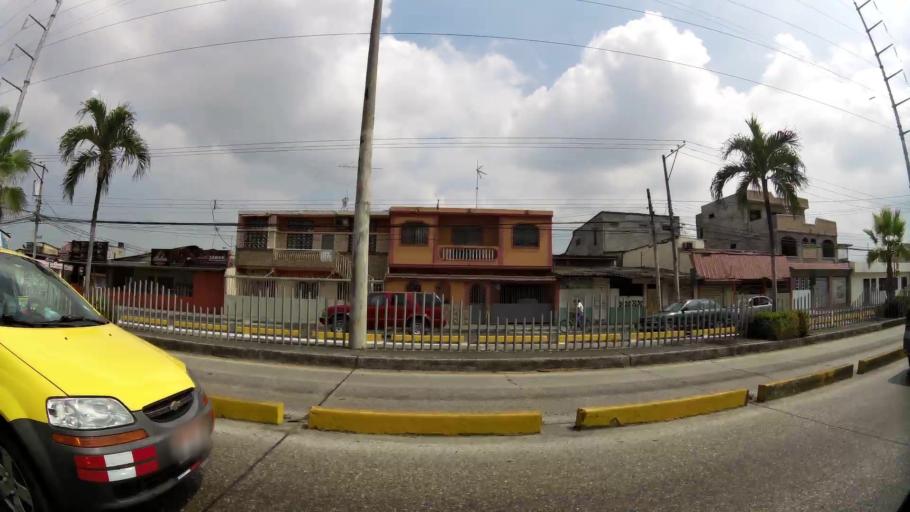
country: EC
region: Guayas
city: Guayaquil
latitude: -2.2332
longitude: -79.8905
